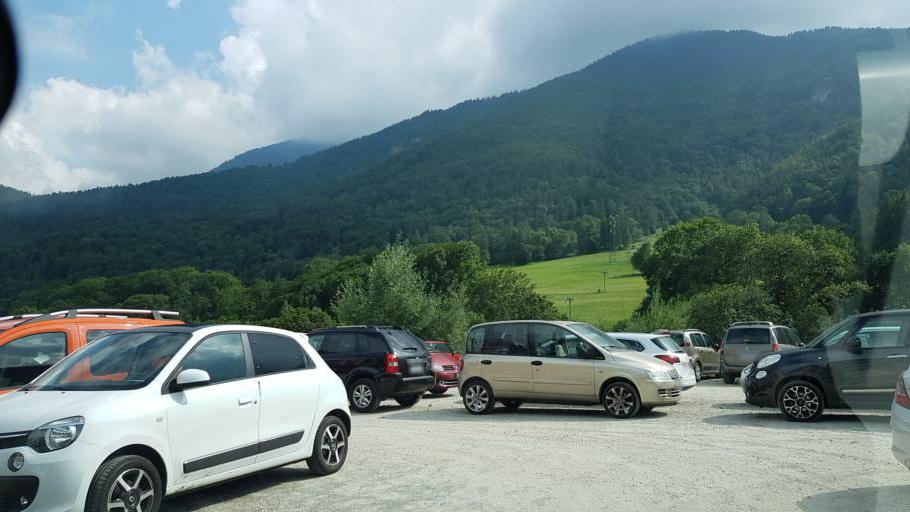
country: IT
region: Piedmont
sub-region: Provincia di Cuneo
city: Sampeyre
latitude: 44.5778
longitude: 7.1885
